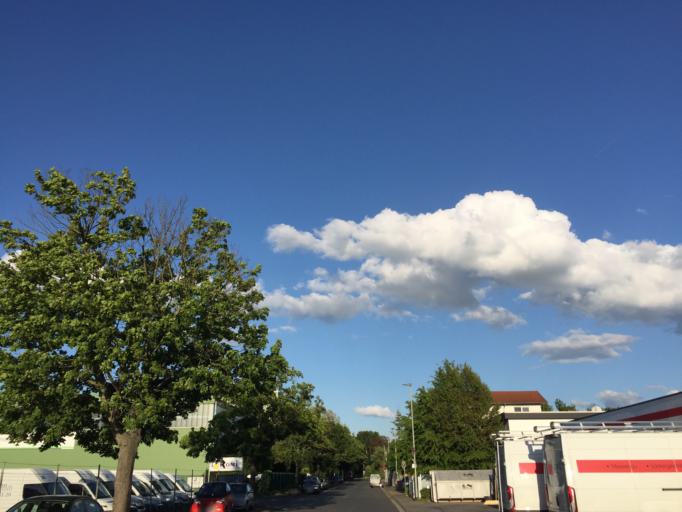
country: DE
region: Hesse
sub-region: Regierungsbezirk Darmstadt
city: Karben
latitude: 50.2285
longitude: 8.7614
